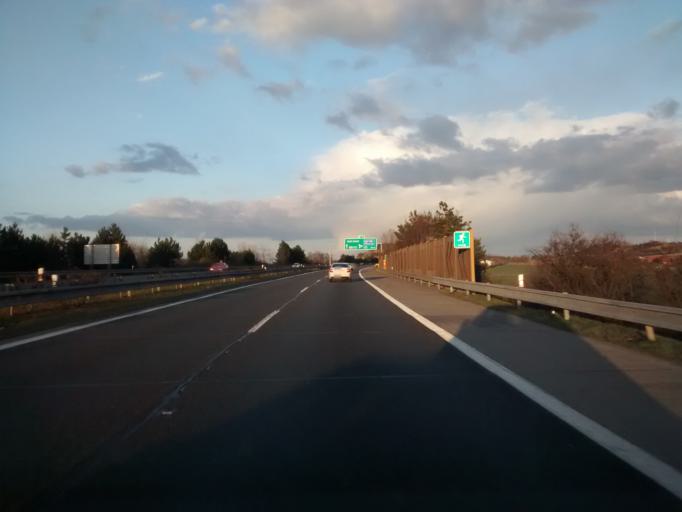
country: CZ
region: Central Bohemia
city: Prerov nad Labem
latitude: 50.1371
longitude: 14.8321
